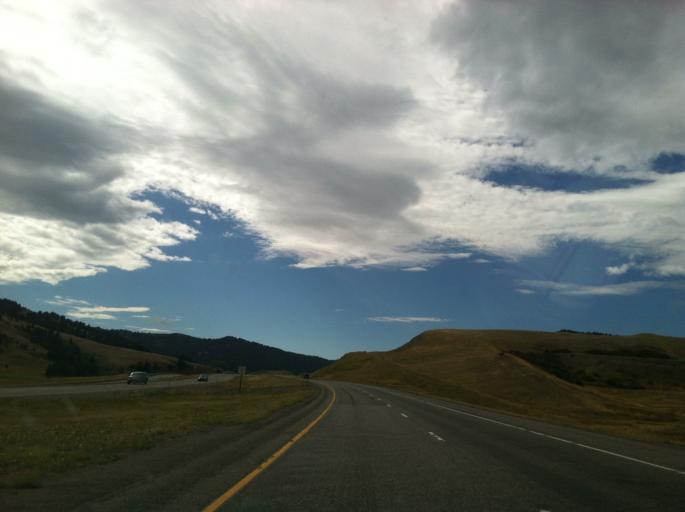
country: US
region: Montana
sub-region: Park County
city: Livingston
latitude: 45.6621
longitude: -110.7277
